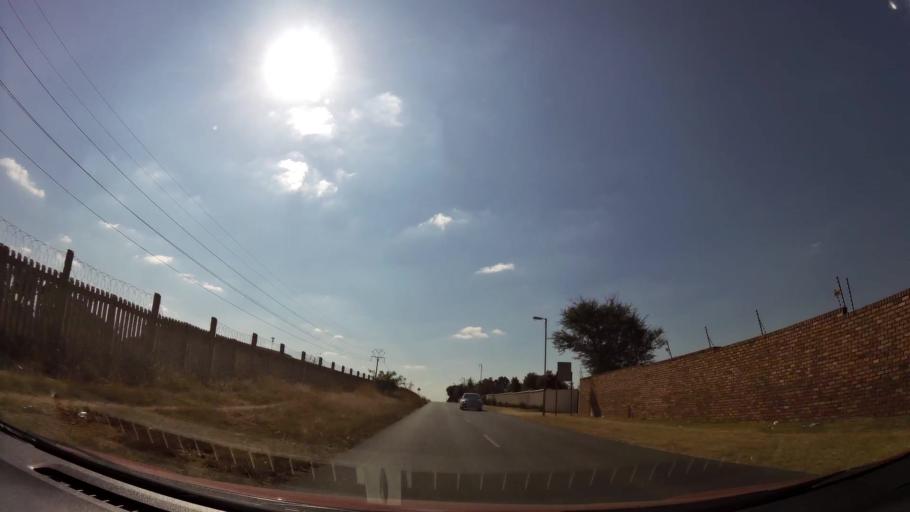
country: ZA
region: Gauteng
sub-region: West Rand District Municipality
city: Muldersdriseloop
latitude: -26.0476
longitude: 27.9298
